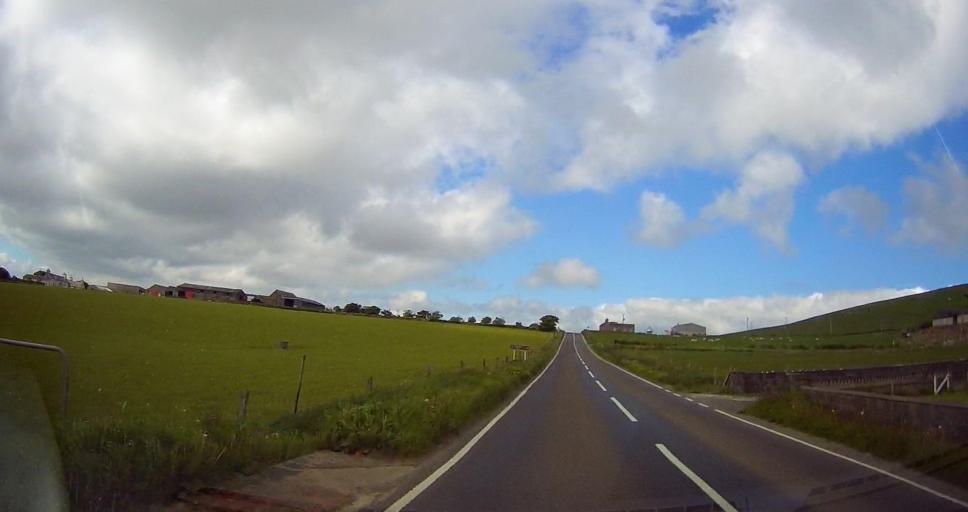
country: GB
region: Scotland
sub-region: Orkney Islands
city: Orkney
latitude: 58.9788
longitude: -3.0182
